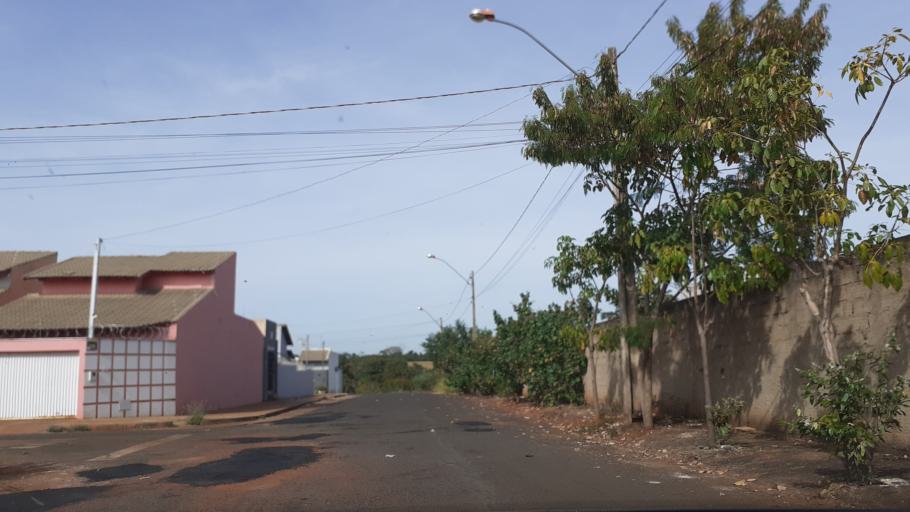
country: BR
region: Goias
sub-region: Itumbiara
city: Itumbiara
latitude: -18.4239
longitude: -49.2459
